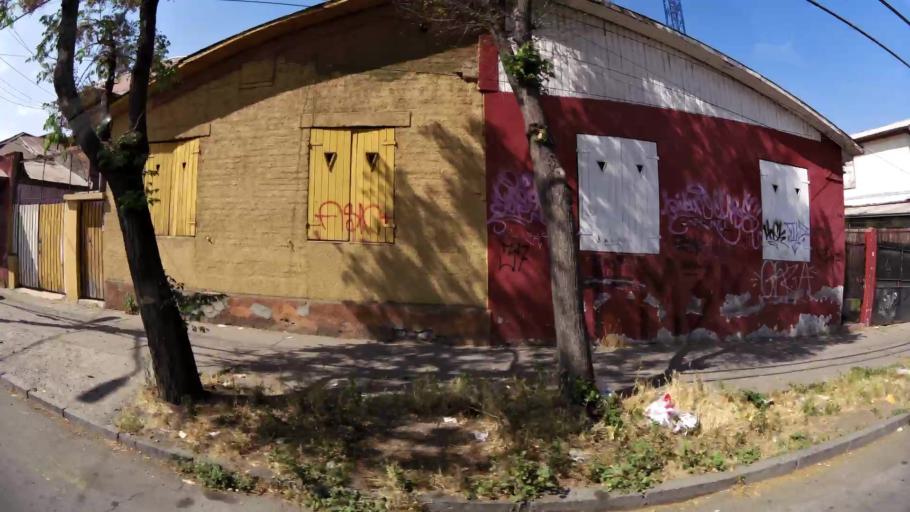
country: CL
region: Santiago Metropolitan
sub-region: Provincia de Santiago
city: Santiago
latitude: -33.4034
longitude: -70.6621
